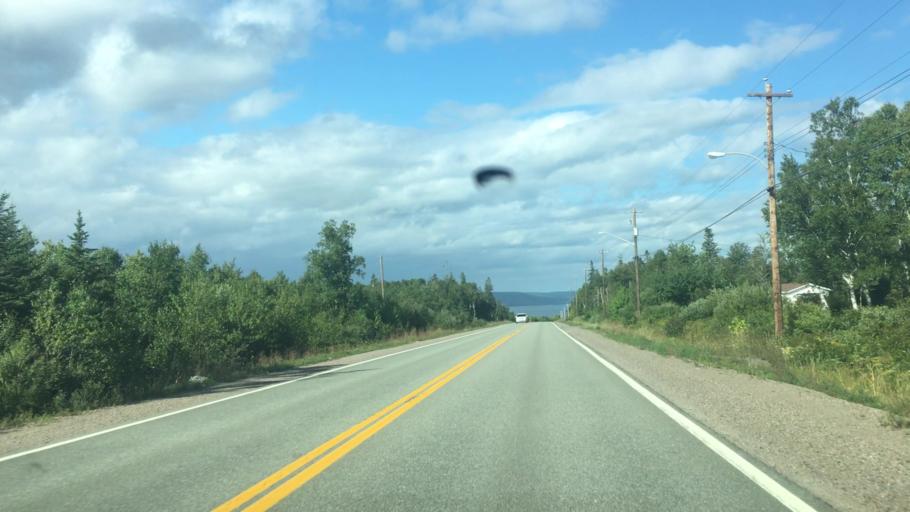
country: CA
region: Nova Scotia
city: Sydney
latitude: 45.8586
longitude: -60.6281
